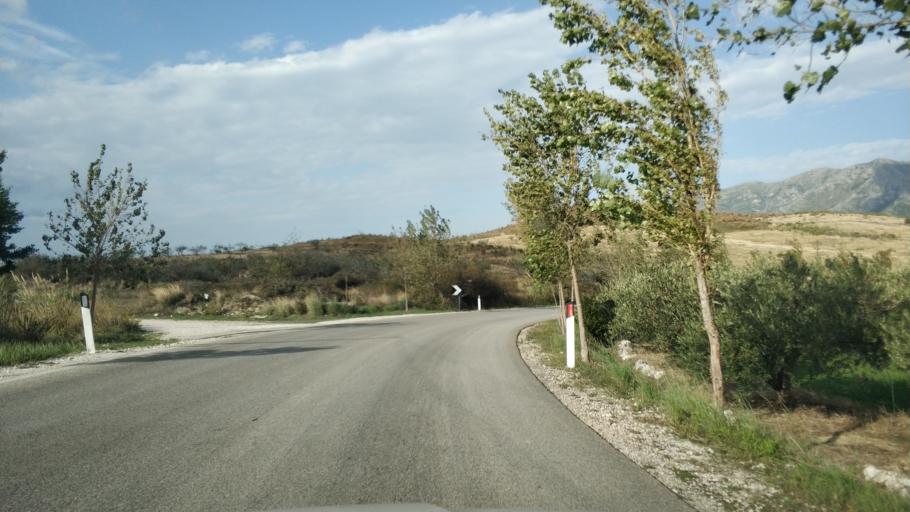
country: AL
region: Vlore
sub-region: Rrethi i Vlores
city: Orikum
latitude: 40.3107
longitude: 19.4800
